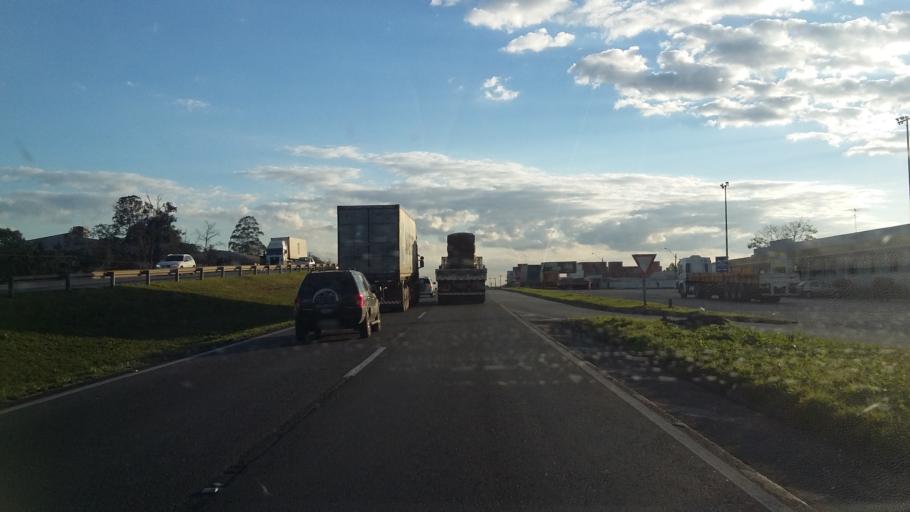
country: BR
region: Parana
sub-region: Campo Largo
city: Campo Largo
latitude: -25.4333
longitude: -49.4067
